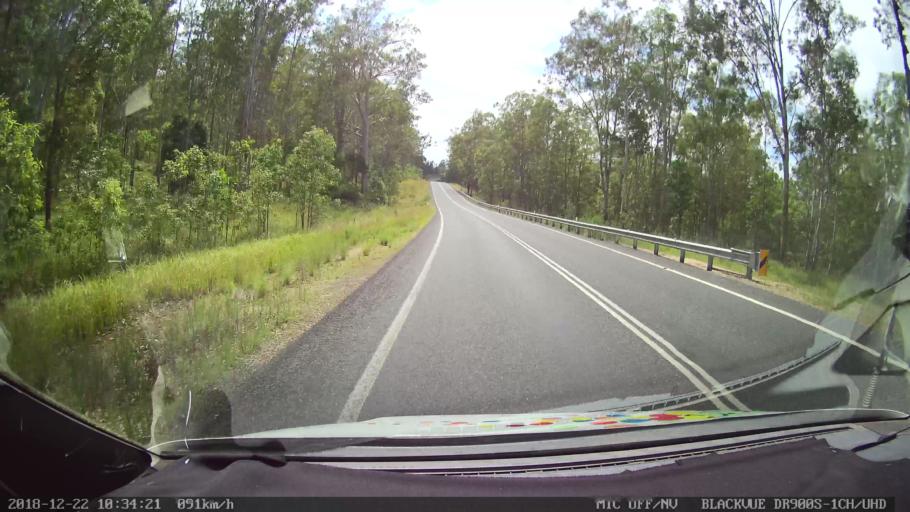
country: AU
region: New South Wales
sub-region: Clarence Valley
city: South Grafton
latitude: -29.6172
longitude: 152.6681
